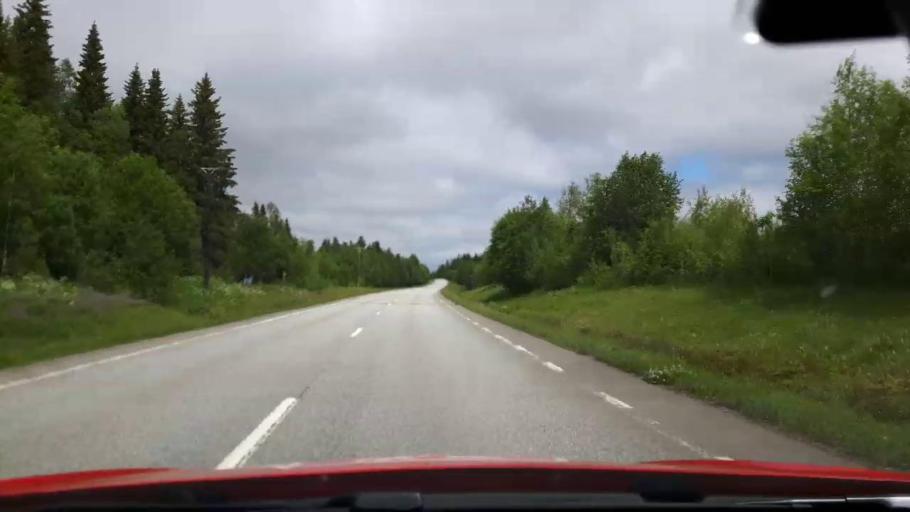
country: SE
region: Jaemtland
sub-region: Krokoms Kommun
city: Krokom
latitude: 63.4958
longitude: 14.5089
